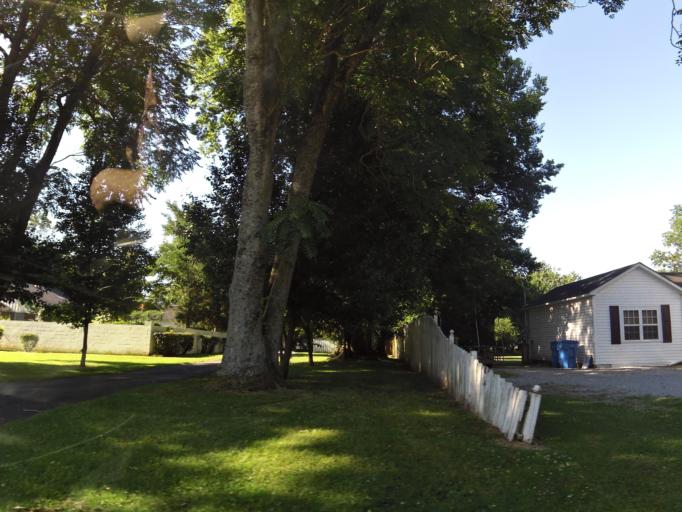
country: US
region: Arkansas
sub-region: Clay County
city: Corning
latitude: 36.4077
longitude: -90.5888
